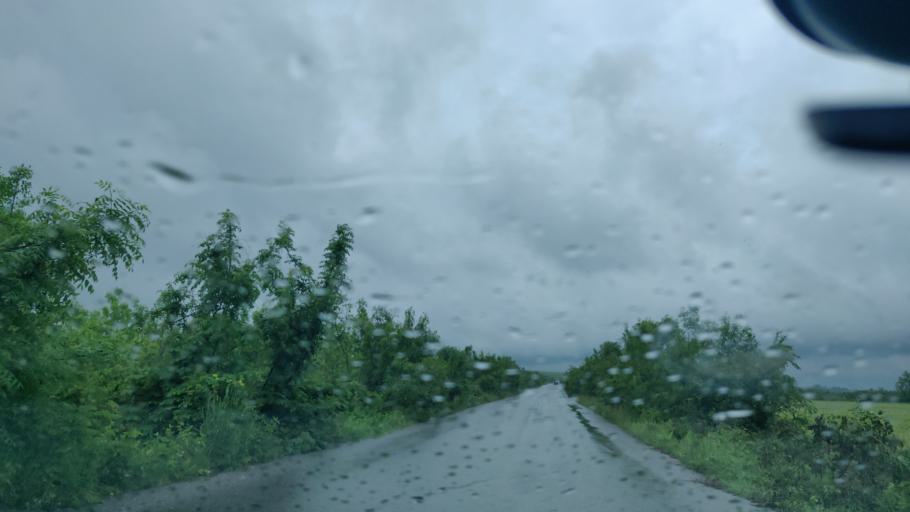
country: RO
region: Giurgiu
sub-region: Comuna Bulbucata
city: Bulbucata
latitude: 44.2905
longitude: 25.7724
